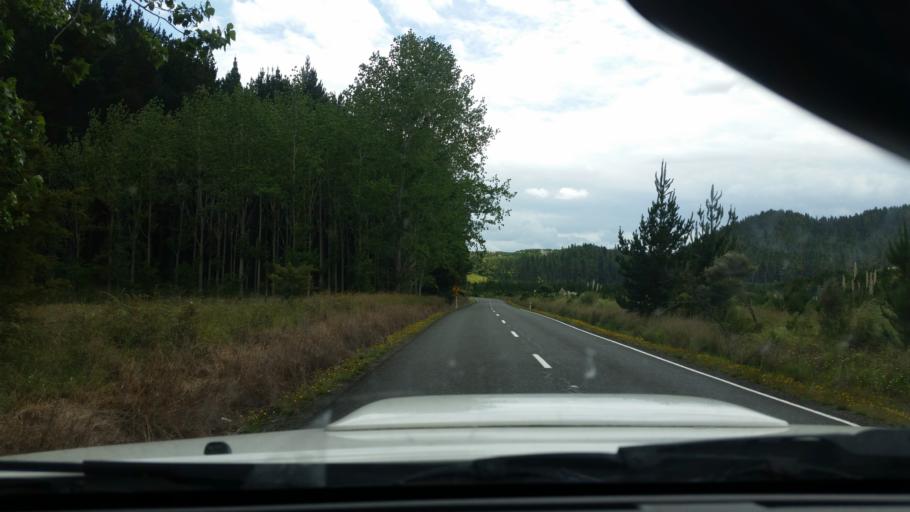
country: NZ
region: Northland
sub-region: Kaipara District
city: Dargaville
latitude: -35.7404
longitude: 173.8741
